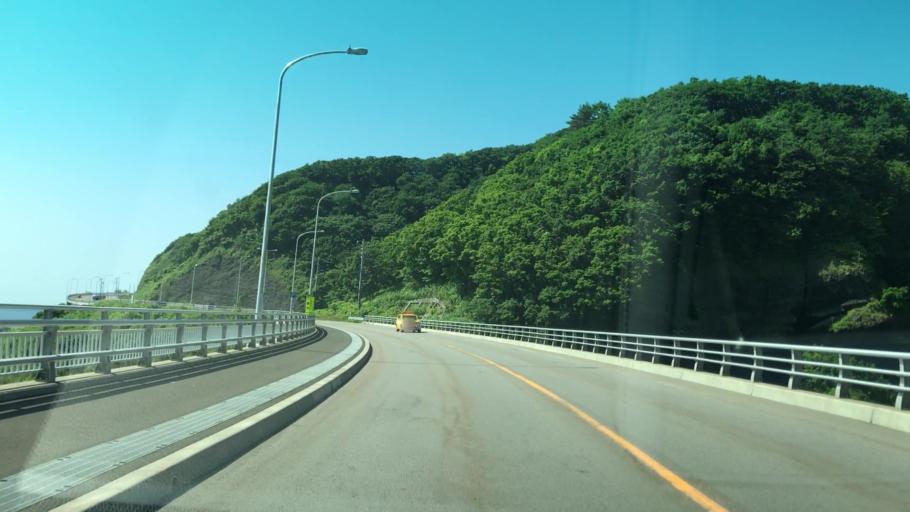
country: JP
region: Hokkaido
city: Iwanai
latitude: 43.1272
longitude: 140.4422
